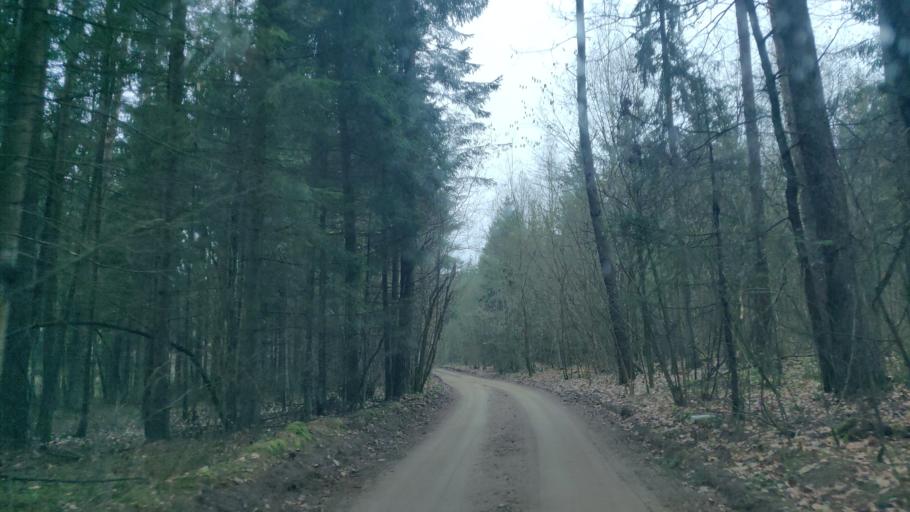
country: LT
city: Trakai
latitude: 54.5564
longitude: 24.9377
